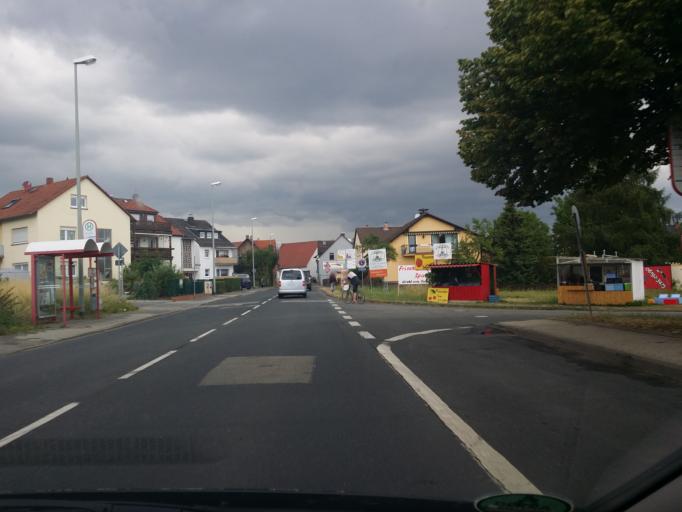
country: DE
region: Hesse
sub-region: Regierungsbezirk Darmstadt
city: Hofheim am Taunus
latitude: 50.0685
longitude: 8.4362
